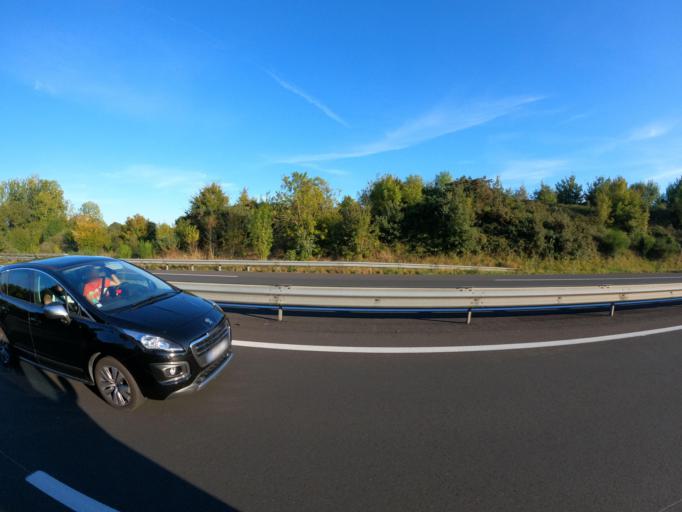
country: FR
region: Pays de la Loire
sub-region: Departement de la Vendee
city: Beaurepaire
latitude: 46.8771
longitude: -1.1129
